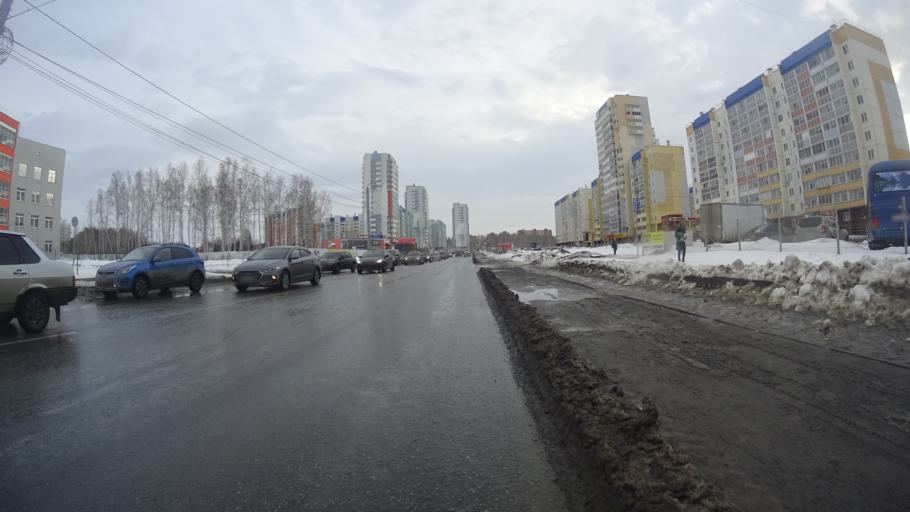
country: RU
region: Chelyabinsk
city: Roshchino
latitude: 55.2060
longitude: 61.2843
